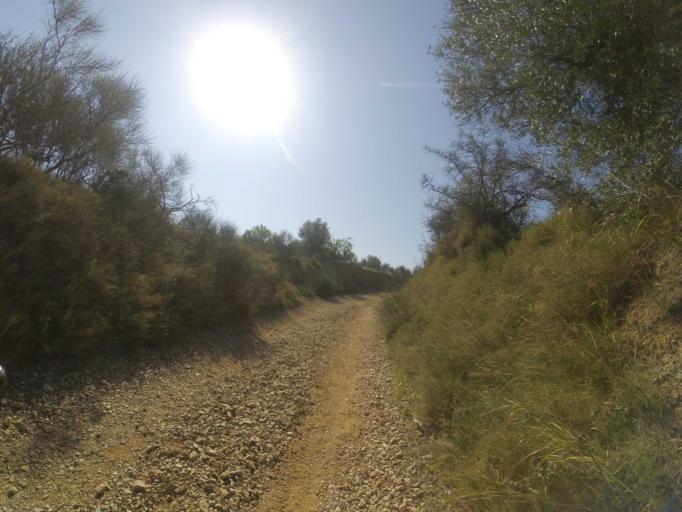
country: FR
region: Languedoc-Roussillon
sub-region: Departement des Pyrenees-Orientales
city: Llupia
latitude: 42.6124
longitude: 2.7638
